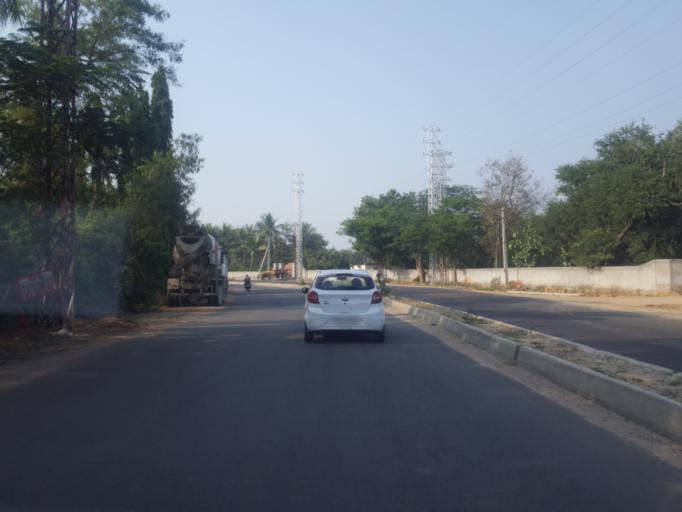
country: IN
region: Telangana
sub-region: Medak
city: Serilingampalle
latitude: 17.3988
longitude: 78.2979
